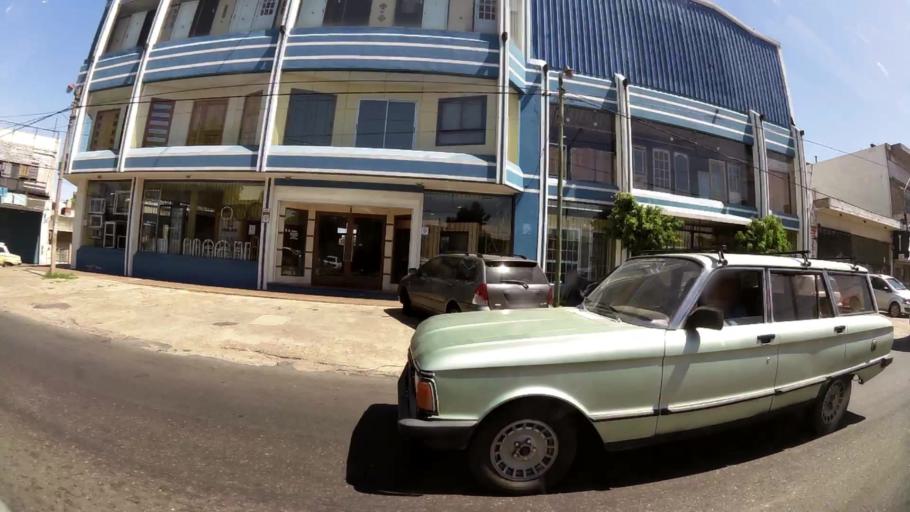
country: AR
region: Buenos Aires
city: Caseros
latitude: -34.5665
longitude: -58.5626
